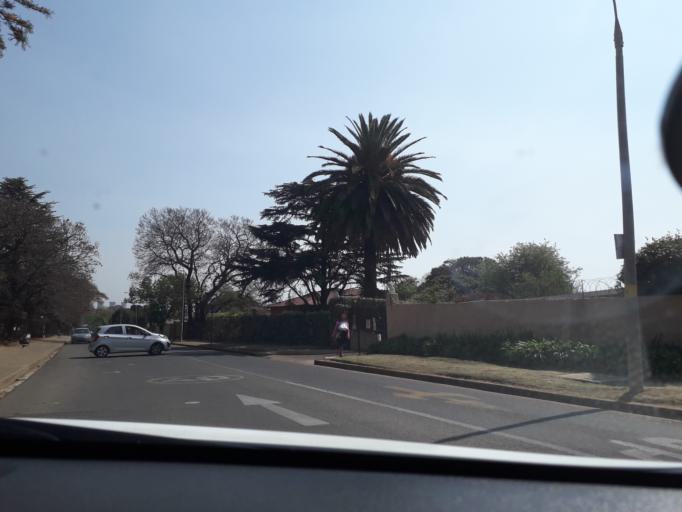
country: ZA
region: Gauteng
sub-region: City of Johannesburg Metropolitan Municipality
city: Modderfontein
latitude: -26.0967
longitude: 28.2265
